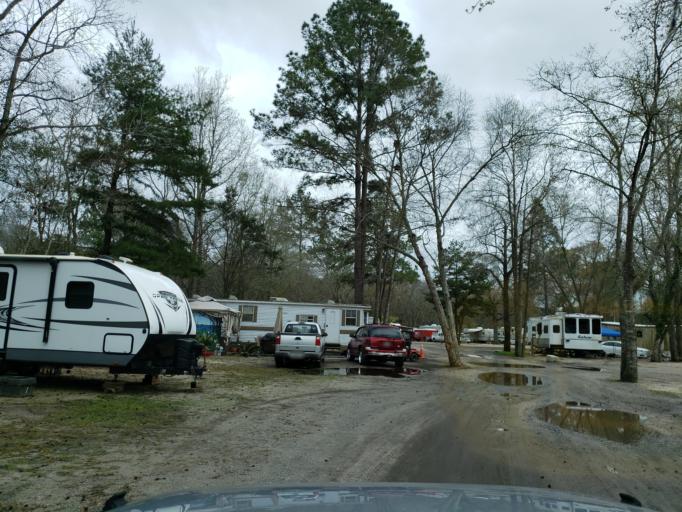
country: US
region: Georgia
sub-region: Chatham County
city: Bloomingdale
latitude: 32.0759
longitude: -81.3732
